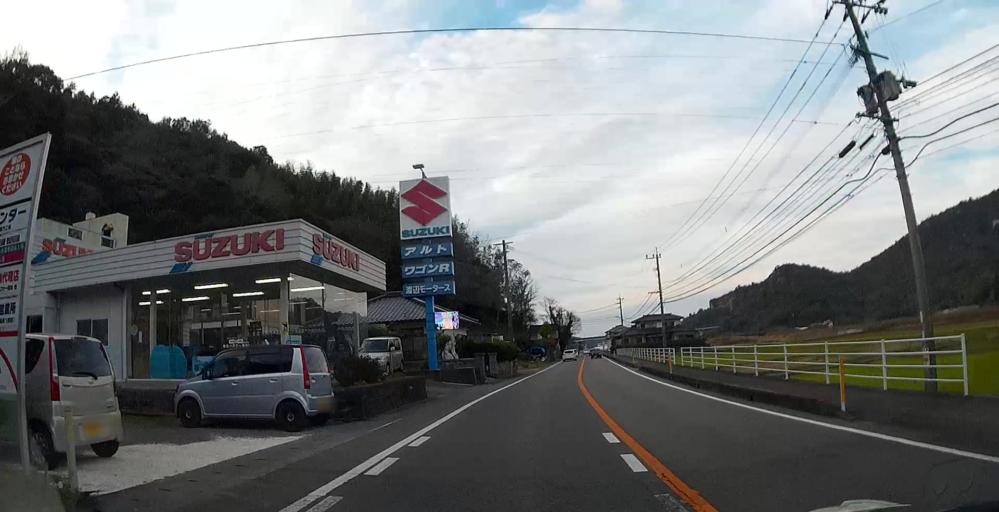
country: JP
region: Kumamoto
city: Yatsushiro
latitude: 32.4981
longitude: 130.4047
